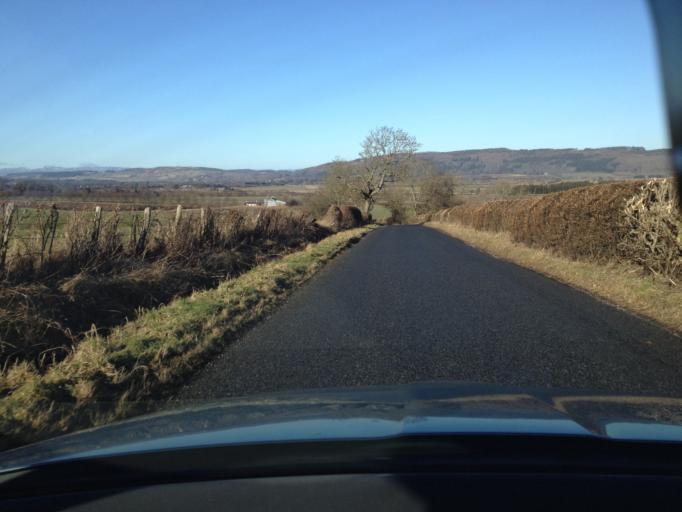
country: GB
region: Scotland
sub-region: Perth and Kinross
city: Bridge of Earn
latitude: 56.3205
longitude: -3.3719
